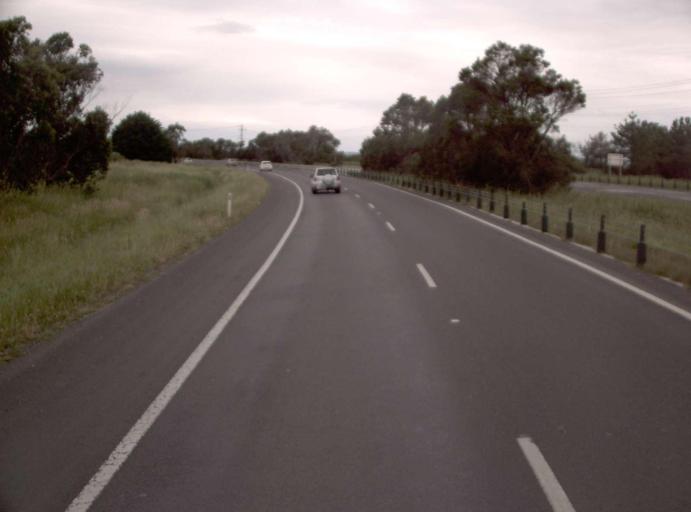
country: AU
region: Victoria
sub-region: Cardinia
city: Koo-Wee-Rup
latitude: -38.2317
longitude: 145.5105
